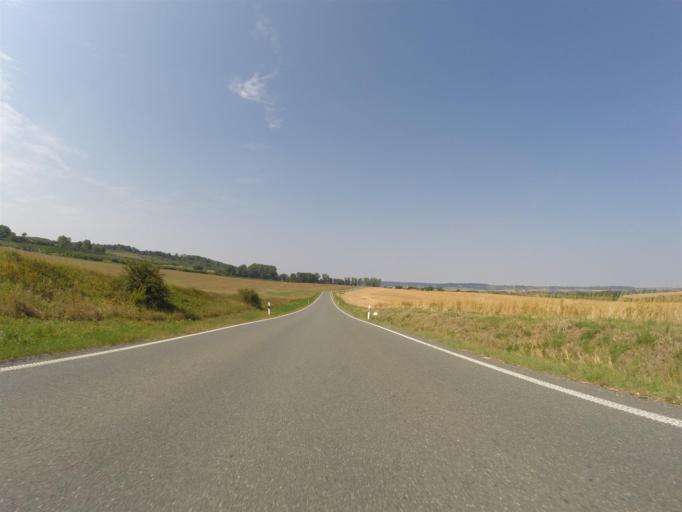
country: DE
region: Thuringia
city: Schongleina
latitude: 50.9137
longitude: 11.7313
